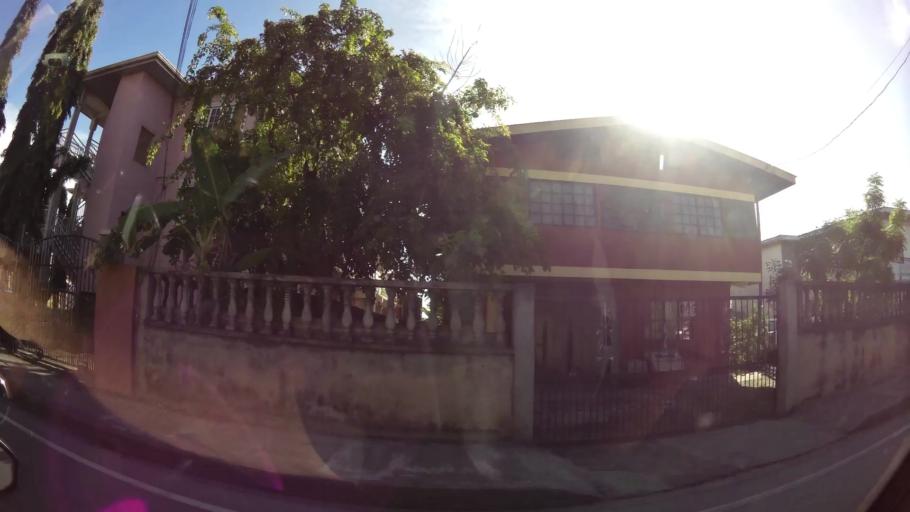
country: TT
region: Chaguanas
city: Chaguanas
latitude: 10.5208
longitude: -61.3789
